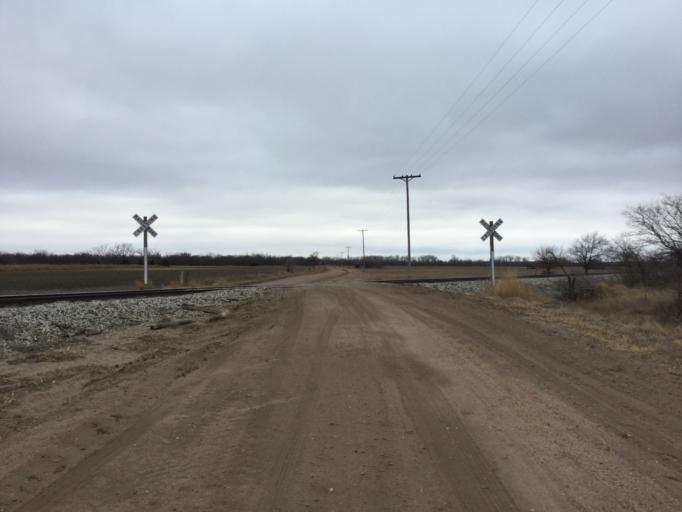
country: US
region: Kansas
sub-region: Barton County
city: Ellinwood
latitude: 38.3037
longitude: -98.4674
